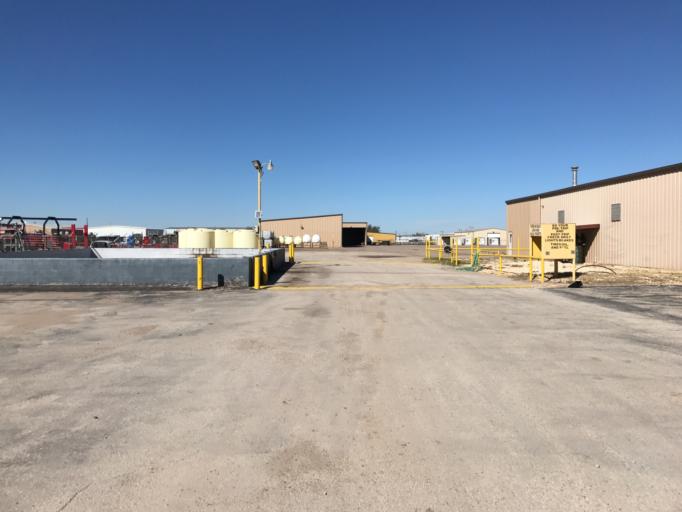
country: US
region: Texas
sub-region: Ector County
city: Odessa
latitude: 31.8984
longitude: -102.2427
